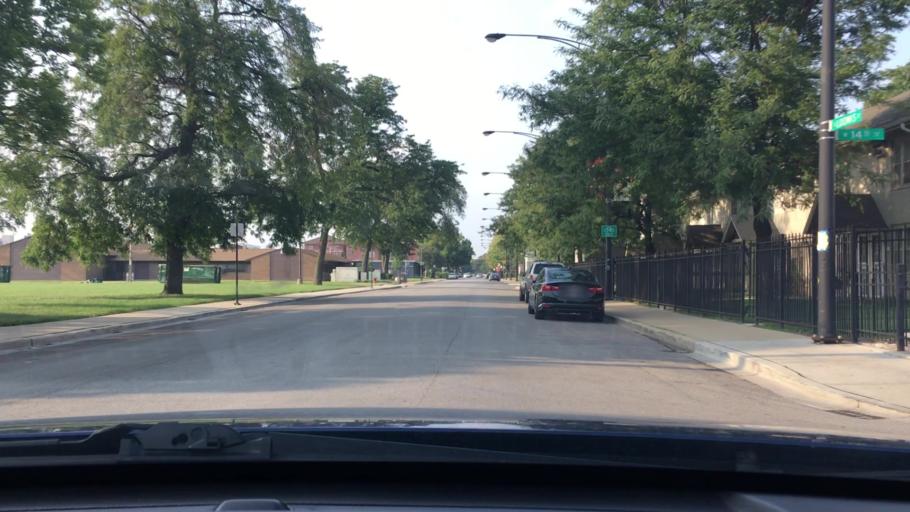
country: US
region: Illinois
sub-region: Cook County
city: Chicago
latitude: 41.8634
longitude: -87.6614
